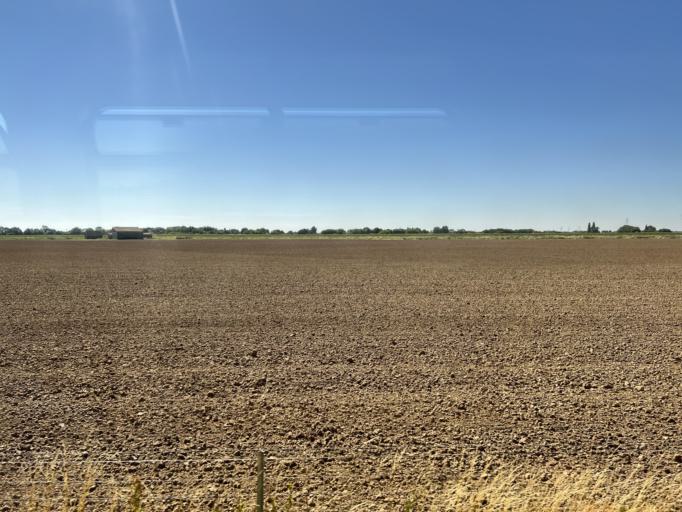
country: GB
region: England
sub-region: Lincolnshire
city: Wainfleet All Saints
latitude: 53.1179
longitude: 0.2072
